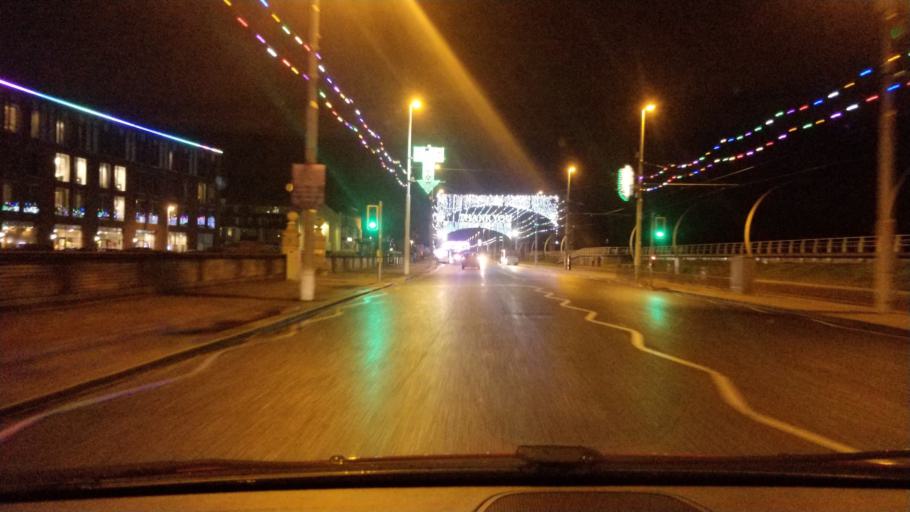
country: GB
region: England
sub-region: Blackpool
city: Blackpool
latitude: 53.7859
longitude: -3.0581
